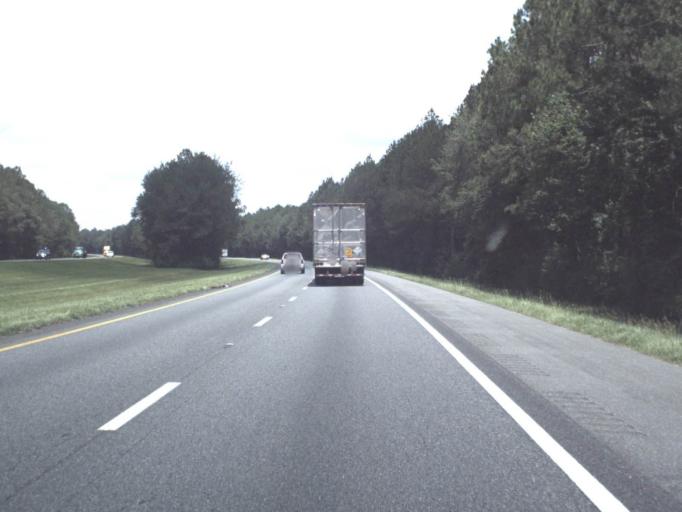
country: US
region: Florida
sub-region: Baker County
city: Macclenny
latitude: 30.2517
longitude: -82.3254
